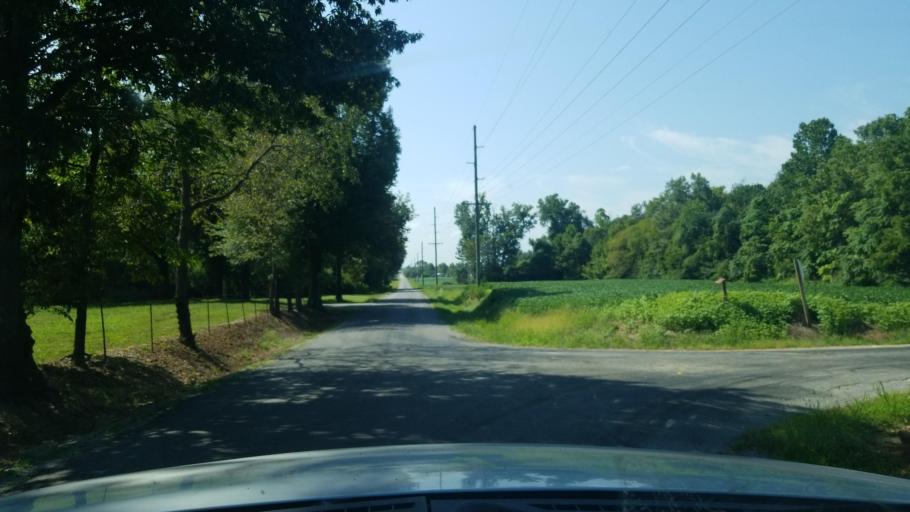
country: US
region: Illinois
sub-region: Saline County
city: Harrisburg
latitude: 37.8496
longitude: -88.6517
